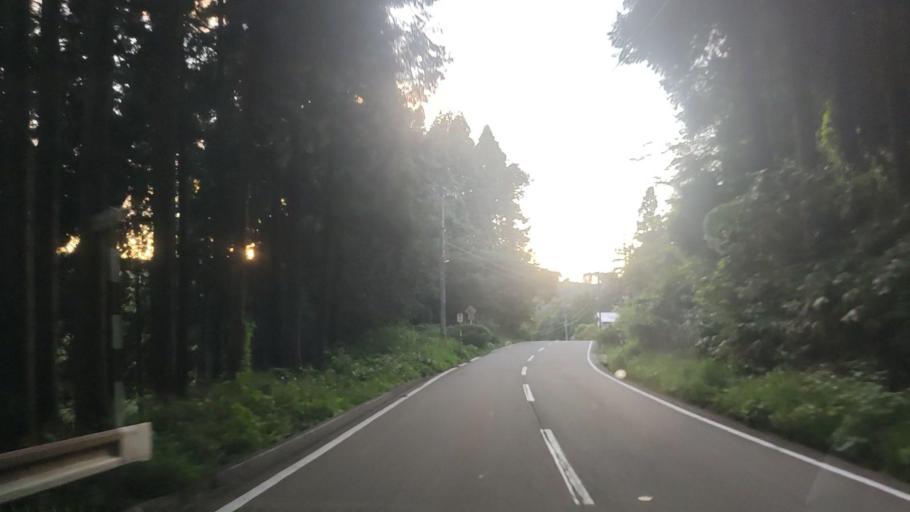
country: JP
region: Ishikawa
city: Tsubata
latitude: 36.6275
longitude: 136.7767
